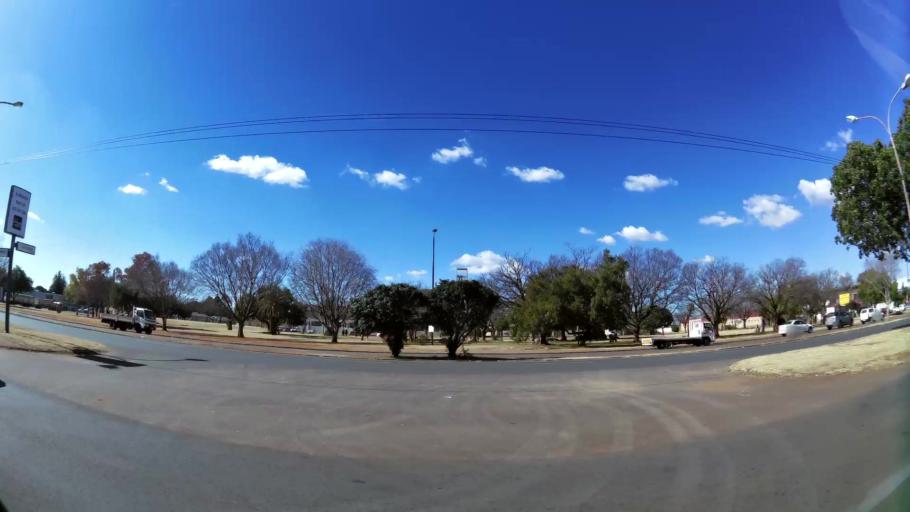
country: ZA
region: Gauteng
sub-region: West Rand District Municipality
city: Carletonville
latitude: -26.3565
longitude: 27.3998
